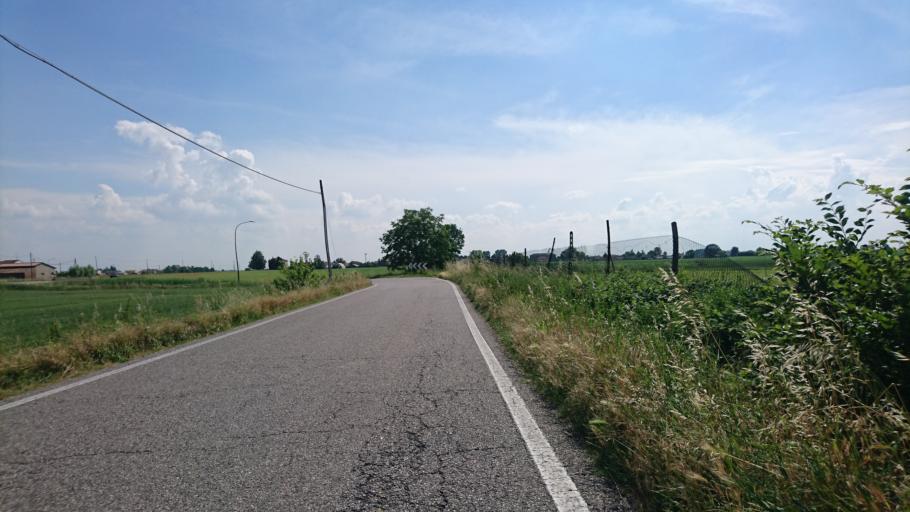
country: IT
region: Veneto
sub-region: Provincia di Rovigo
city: Castelmassa
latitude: 45.0669
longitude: 11.3346
